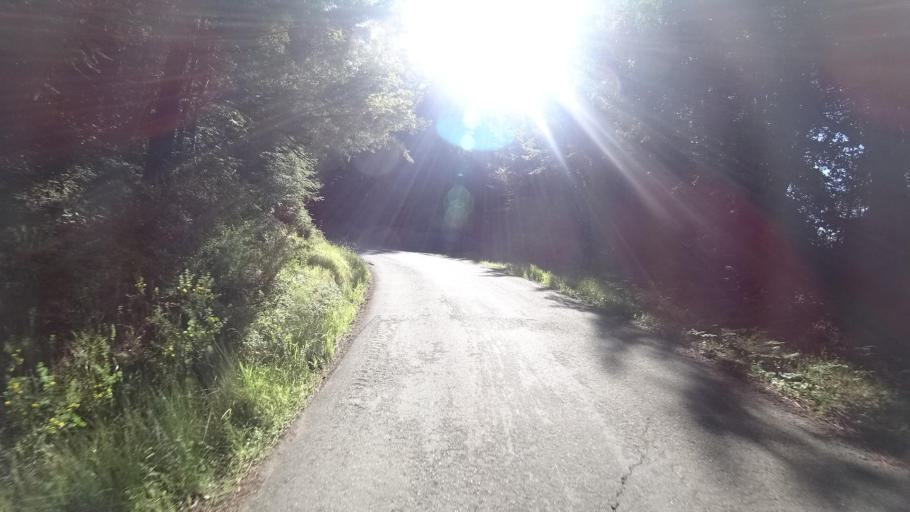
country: US
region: California
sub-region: Humboldt County
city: Rio Dell
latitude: 40.4603
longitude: -123.9991
